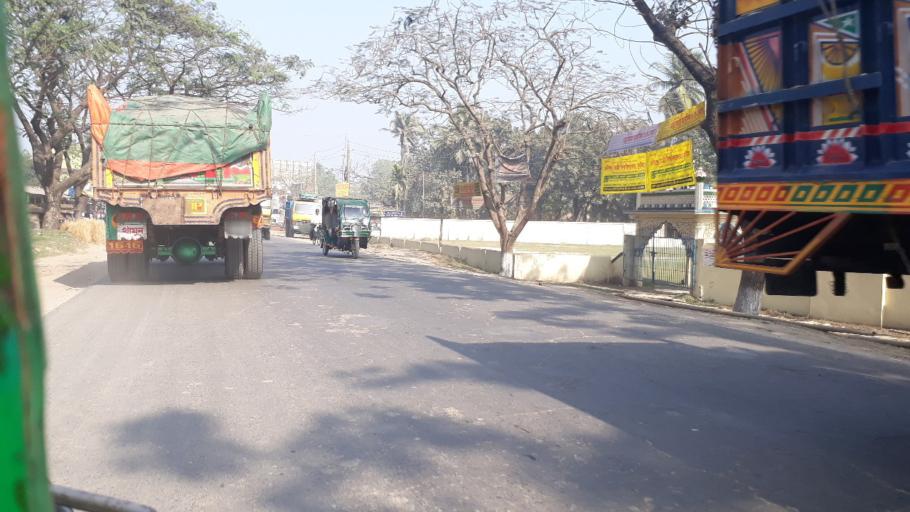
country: BD
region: Khulna
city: Kushtia
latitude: 23.8891
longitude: 89.1087
